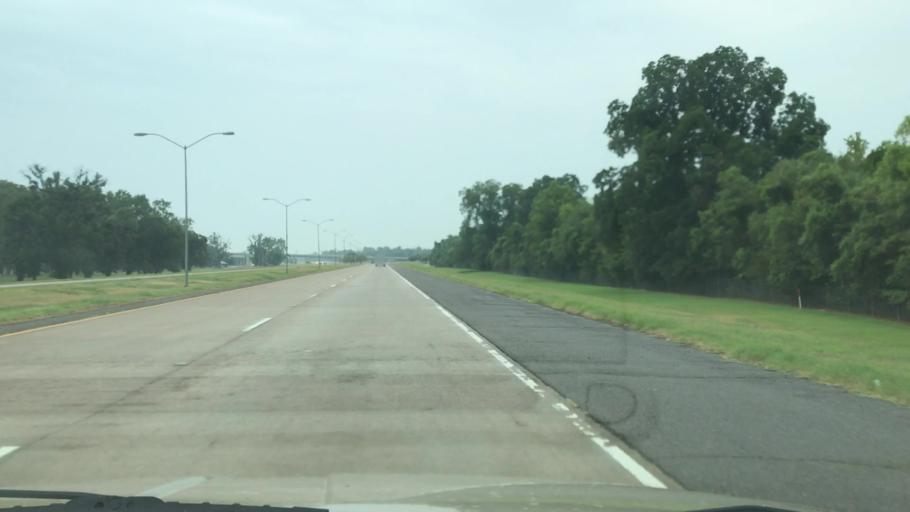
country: US
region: Louisiana
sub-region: Bossier Parish
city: Bossier City
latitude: 32.4872
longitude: -93.6888
